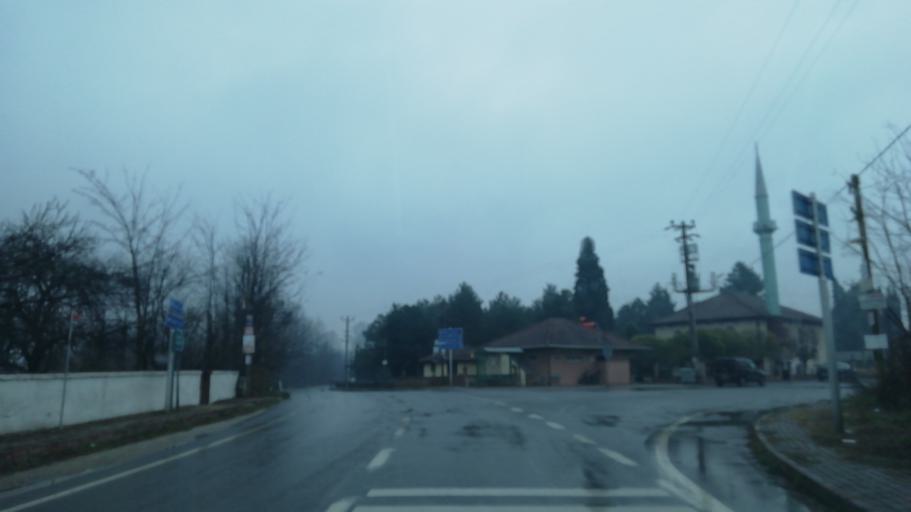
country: TR
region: Sakarya
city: Karapurcek
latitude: 40.6715
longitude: 30.5669
